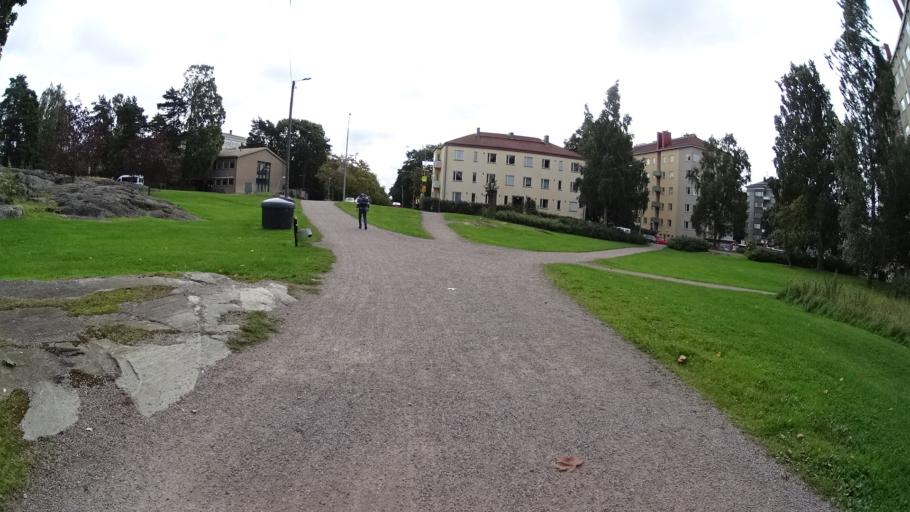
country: FI
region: Uusimaa
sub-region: Helsinki
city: Helsinki
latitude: 60.1922
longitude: 24.9133
